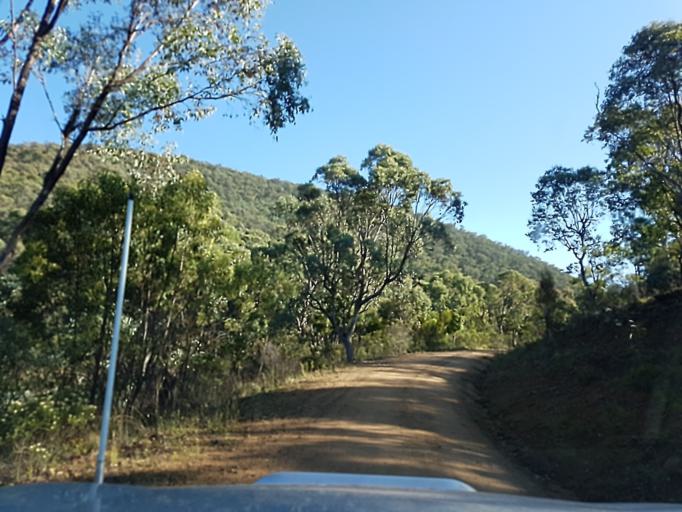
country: AU
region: New South Wales
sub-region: Snowy River
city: Jindabyne
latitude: -36.9346
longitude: 148.3397
